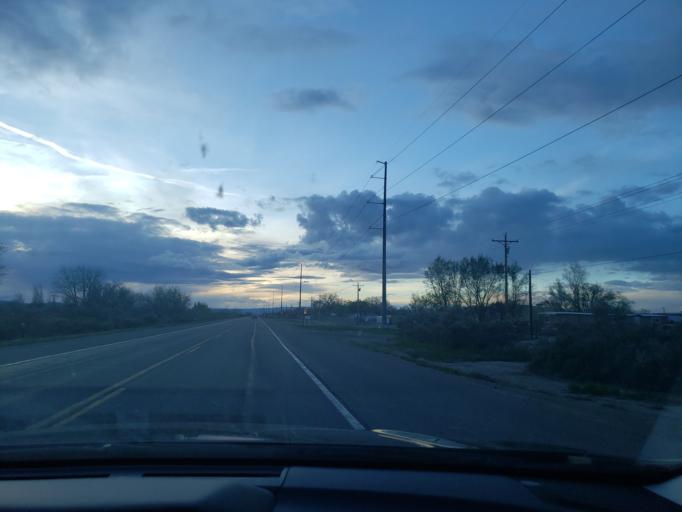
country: US
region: Colorado
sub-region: Mesa County
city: Redlands
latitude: 39.1259
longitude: -108.6756
